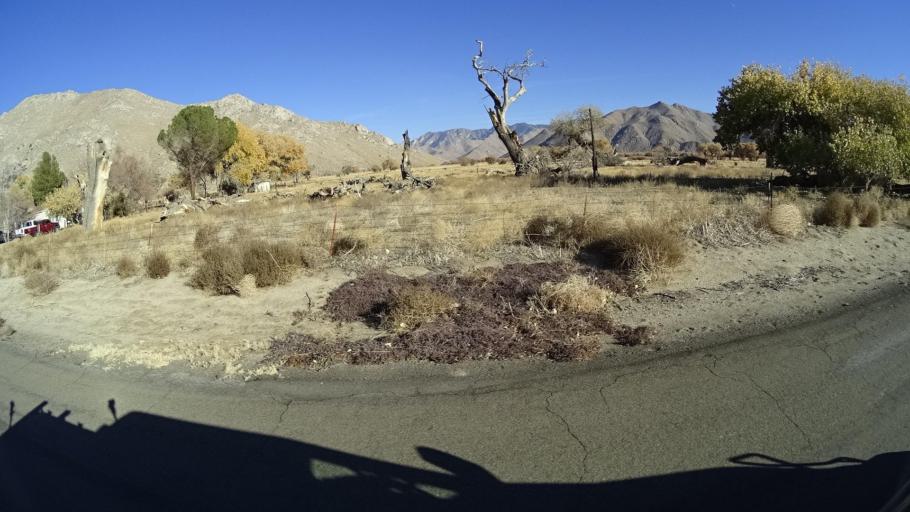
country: US
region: California
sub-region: Kern County
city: Weldon
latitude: 35.6864
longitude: -118.2902
